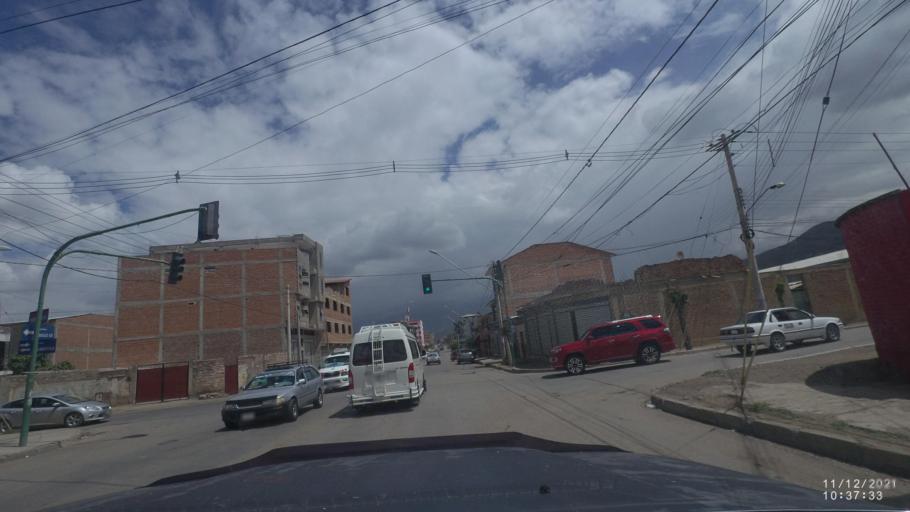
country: BO
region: Cochabamba
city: Cochabamba
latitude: -17.4449
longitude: -66.1251
